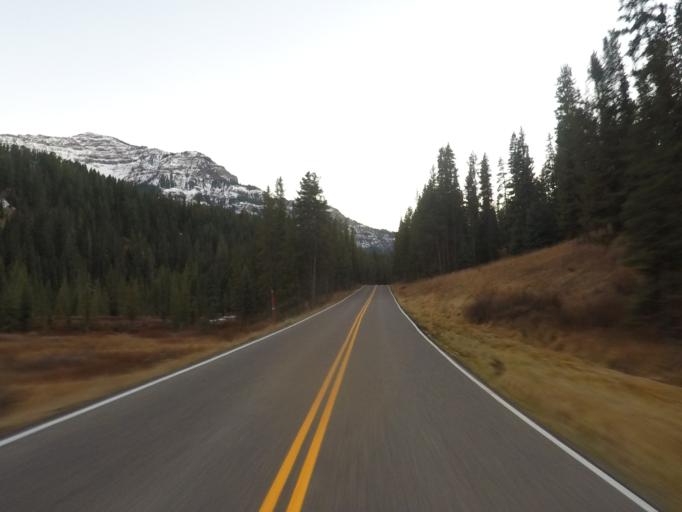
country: US
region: Montana
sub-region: Stillwater County
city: Absarokee
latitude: 44.9341
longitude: -110.0841
